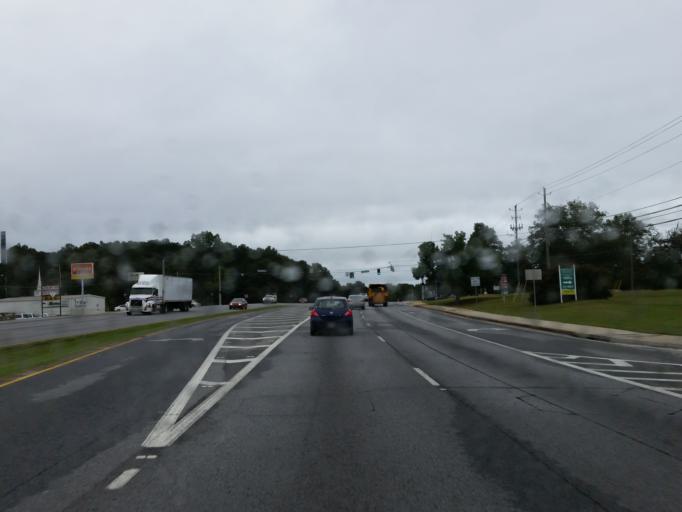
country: US
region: Georgia
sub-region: Clayton County
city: Lovejoy
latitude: 33.4419
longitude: -84.3221
